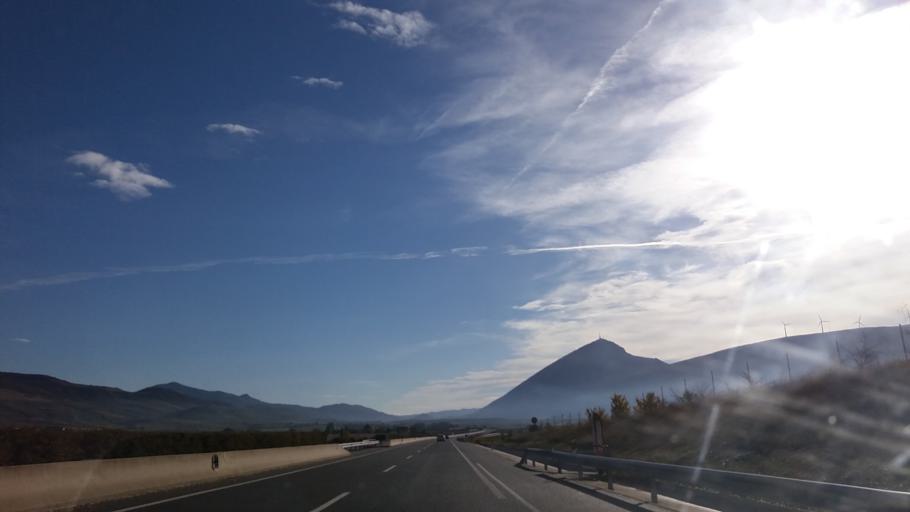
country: ES
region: Navarre
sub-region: Provincia de Navarra
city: Elorz
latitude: 42.7446
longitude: -1.5934
